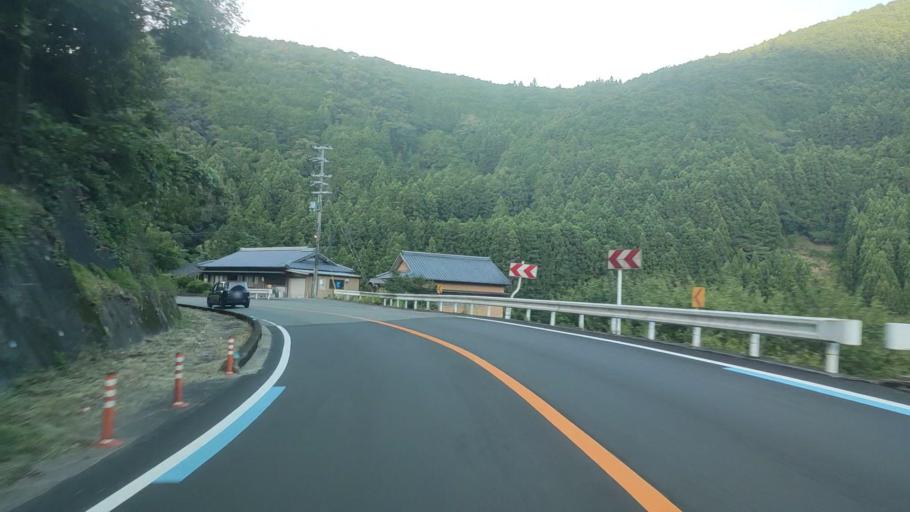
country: JP
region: Wakayama
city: Tanabe
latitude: 33.8109
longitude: 135.5496
